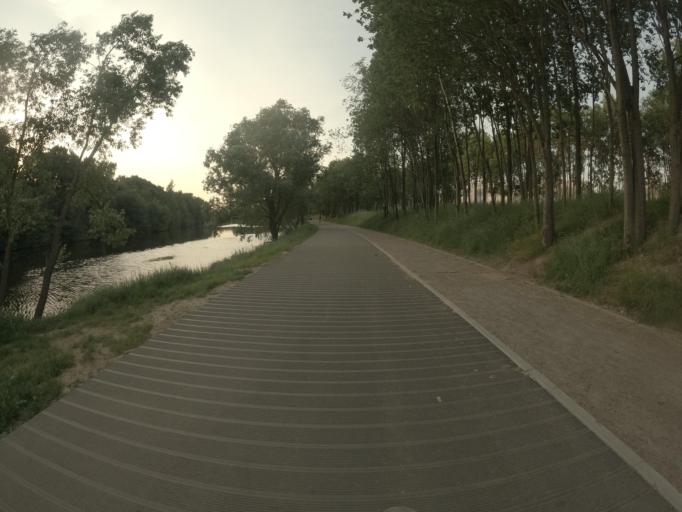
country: RU
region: St.-Petersburg
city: Krasnogvargeisky
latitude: 59.9440
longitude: 30.4569
